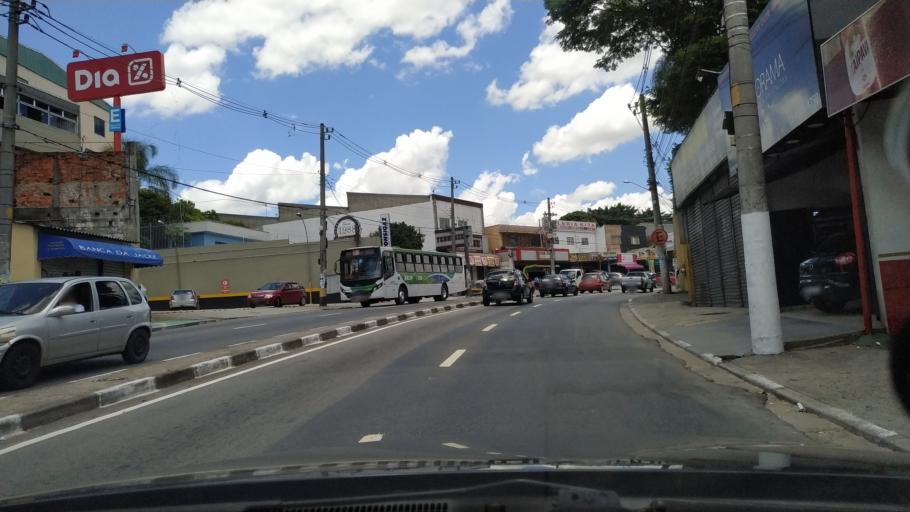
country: BR
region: Sao Paulo
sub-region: Barueri
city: Barueri
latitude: -23.4918
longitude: -46.8814
